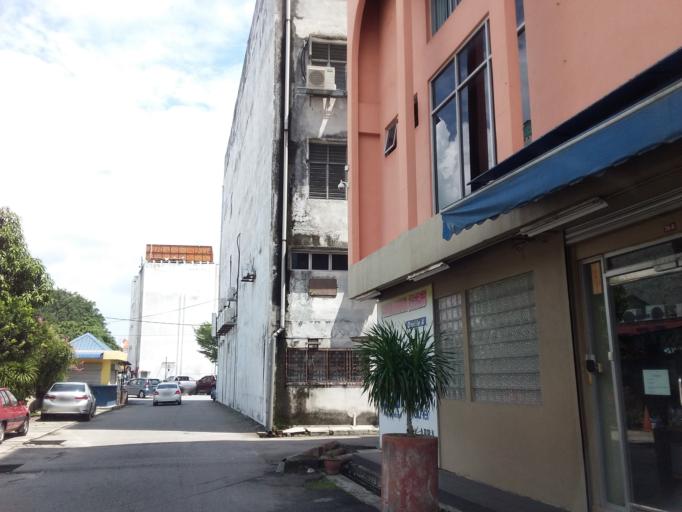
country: MY
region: Johor
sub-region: Daerah Batu Pahat
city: Batu Pahat
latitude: 1.8540
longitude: 102.9275
